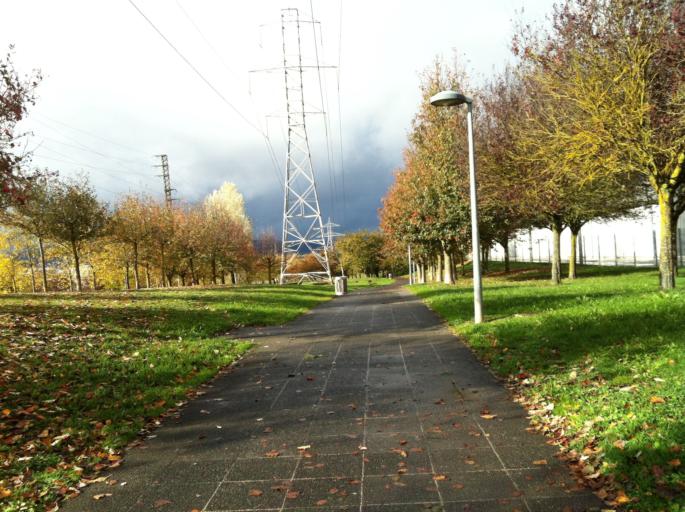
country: ES
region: Basque Country
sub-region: Provincia de Alava
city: Gasteiz / Vitoria
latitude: 42.8646
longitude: -2.7040
